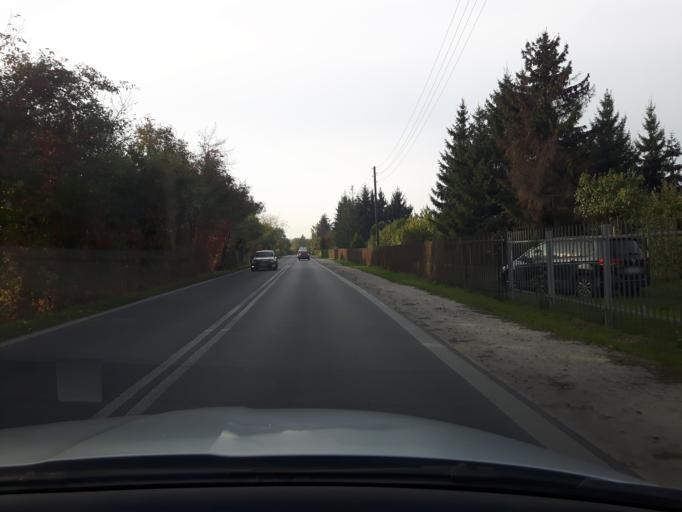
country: PL
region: Masovian Voivodeship
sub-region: Powiat wolominski
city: Zabki
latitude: 52.2832
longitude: 21.0965
